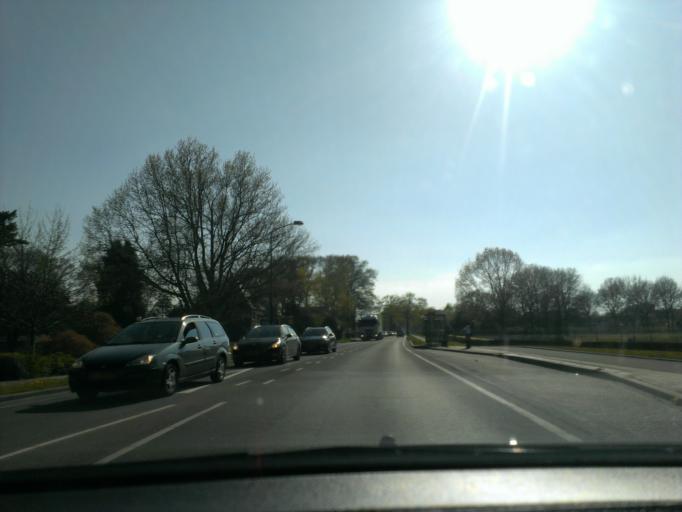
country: NL
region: Gelderland
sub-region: Gemeente Apeldoorn
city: Apeldoorn
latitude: 52.2252
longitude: 6.0112
